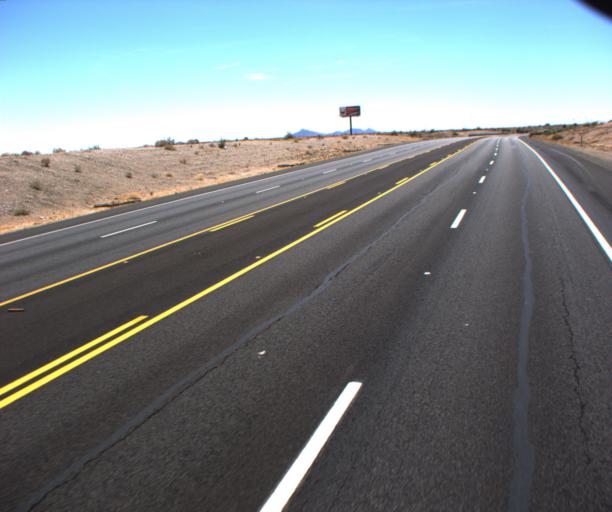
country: US
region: Arizona
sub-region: La Paz County
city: Cienega Springs
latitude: 34.1693
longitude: -114.2514
